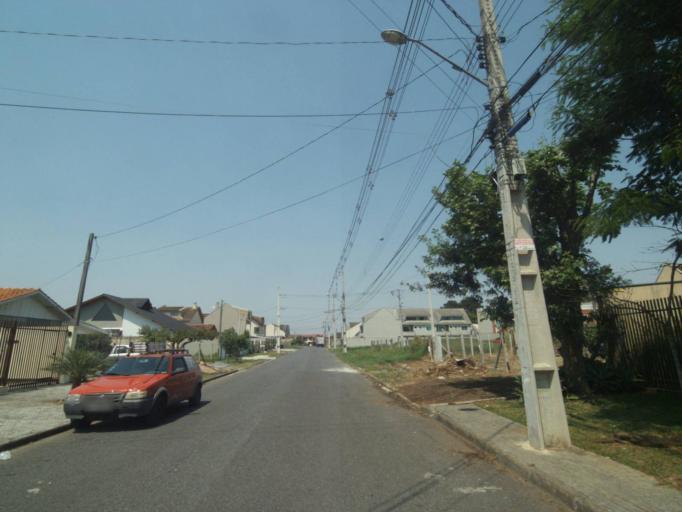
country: BR
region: Parana
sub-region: Sao Jose Dos Pinhais
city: Sao Jose dos Pinhais
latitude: -25.5018
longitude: -49.2706
